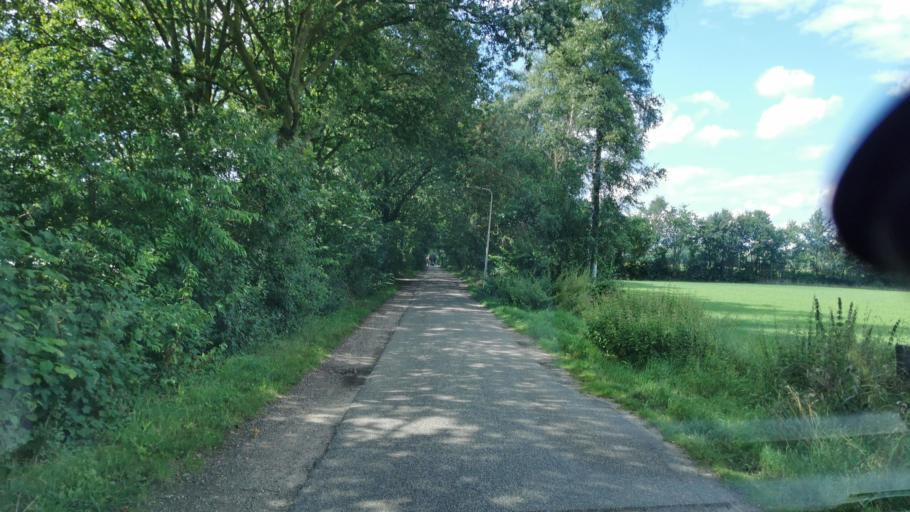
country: DE
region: North Rhine-Westphalia
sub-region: Regierungsbezirk Munster
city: Gronau
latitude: 52.2410
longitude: 7.0398
